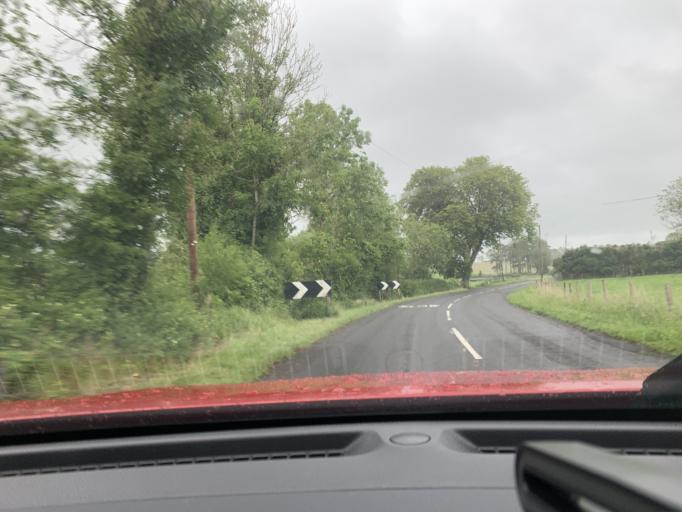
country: GB
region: Northern Ireland
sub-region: Fermanagh District
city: Enniskillen
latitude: 54.3084
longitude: -7.6858
